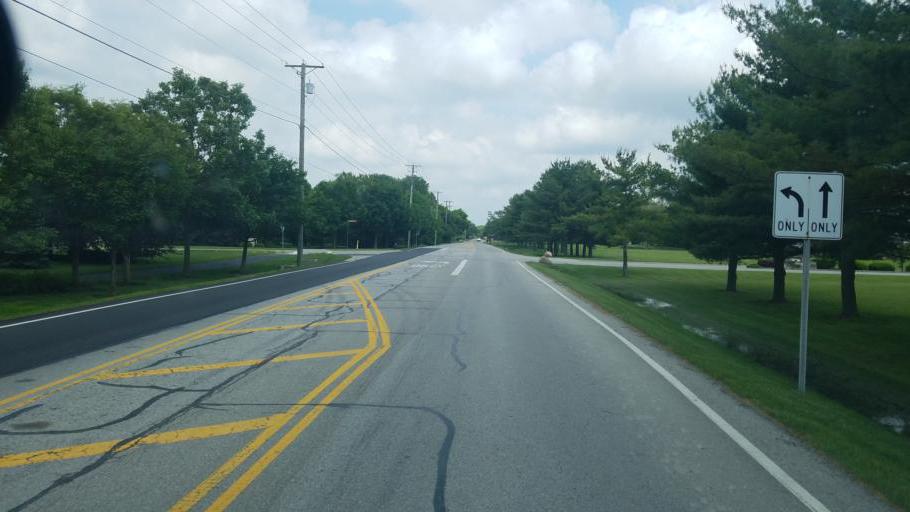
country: US
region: Ohio
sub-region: Franklin County
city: Hilliard
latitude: 40.0771
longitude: -83.1635
